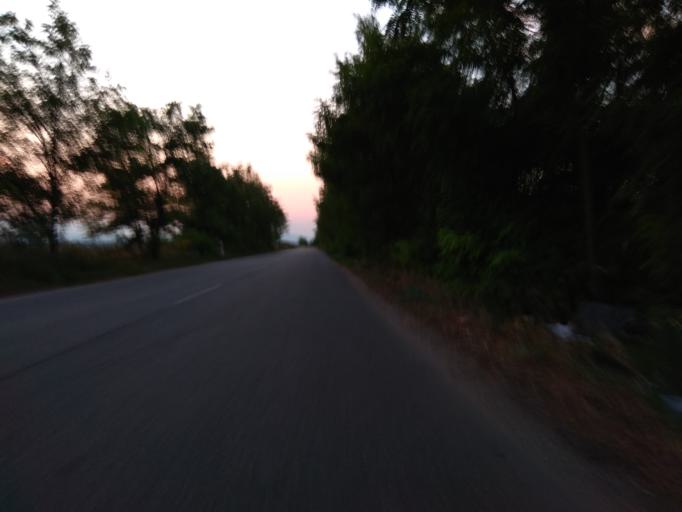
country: HU
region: Borsod-Abauj-Zemplen
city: Emod
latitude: 47.9204
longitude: 20.8415
